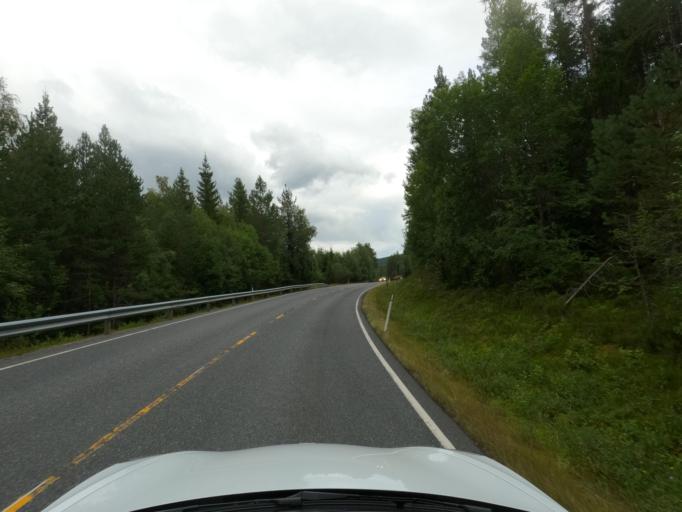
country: NO
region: Telemark
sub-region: Notodden
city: Notodden
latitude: 59.7308
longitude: 9.3467
